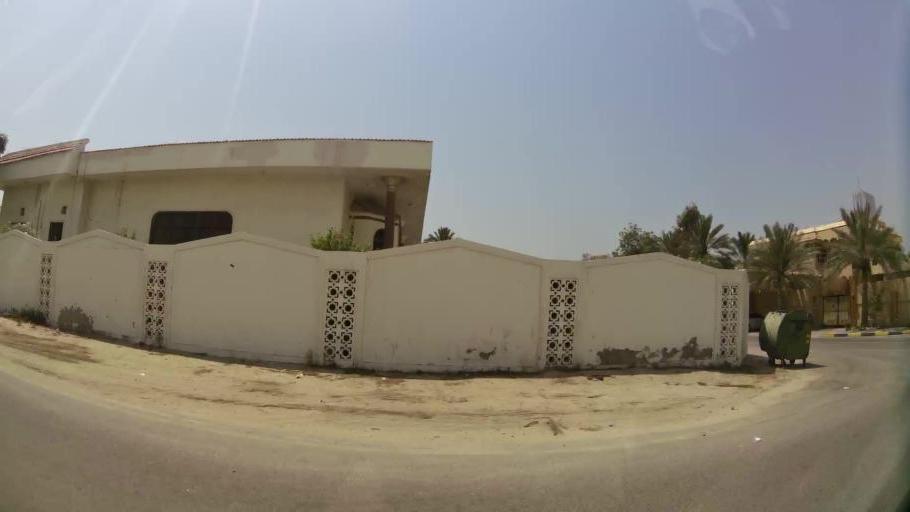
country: AE
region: Ajman
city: Ajman
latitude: 25.3958
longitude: 55.4281
